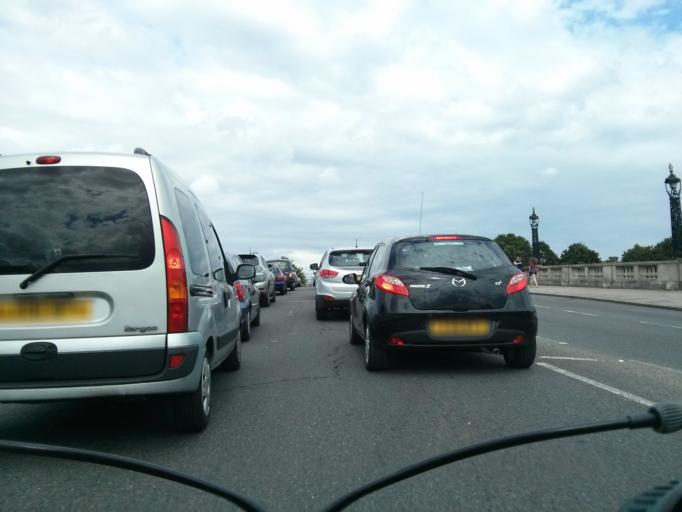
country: GB
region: England
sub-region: Surrey
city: East Molesey
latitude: 51.4032
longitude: -0.3429
